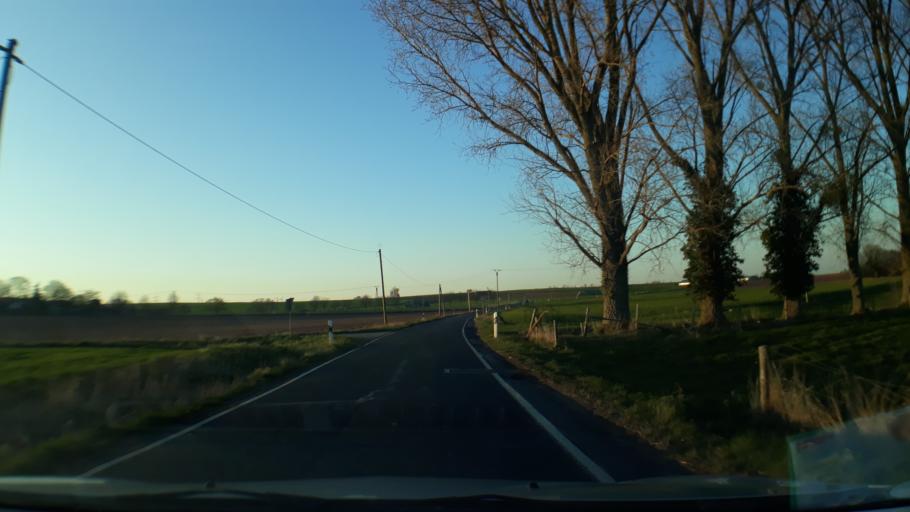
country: DE
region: North Rhine-Westphalia
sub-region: Regierungsbezirk Koln
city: Mechernich
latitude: 50.6087
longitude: 6.5967
